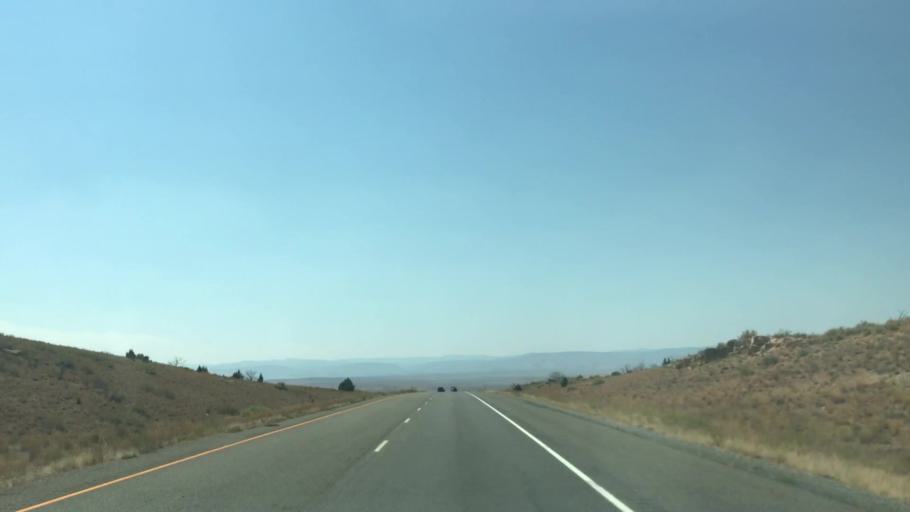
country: US
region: Colorado
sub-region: Mesa County
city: Loma
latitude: 39.1900
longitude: -109.0400
